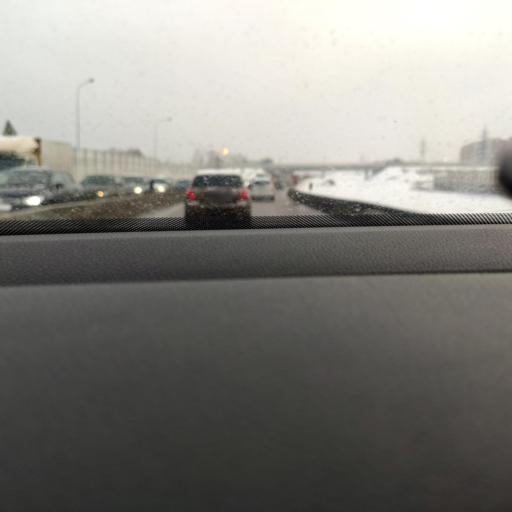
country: RU
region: Moskovskaya
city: Tomilino
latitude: 55.6306
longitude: 37.9368
